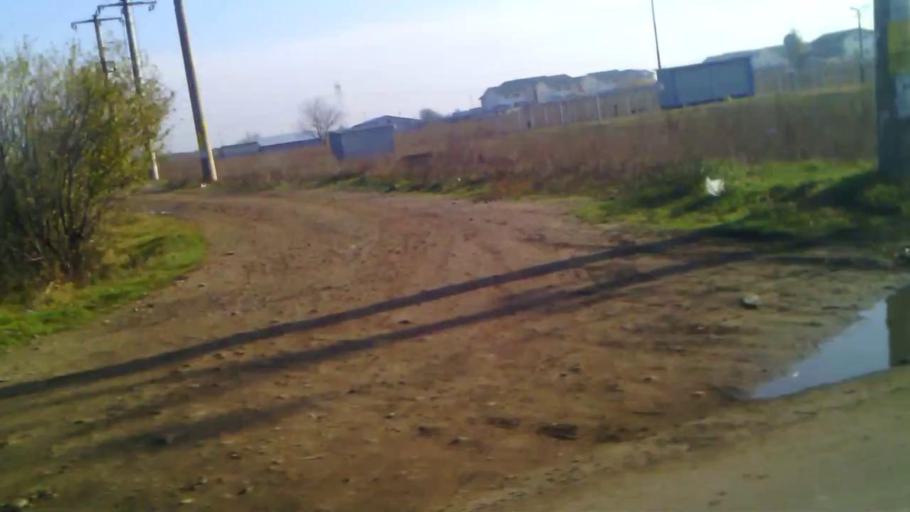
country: RO
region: Ilfov
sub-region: Comuna Berceni
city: Berceni
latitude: 44.3349
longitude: 26.1692
